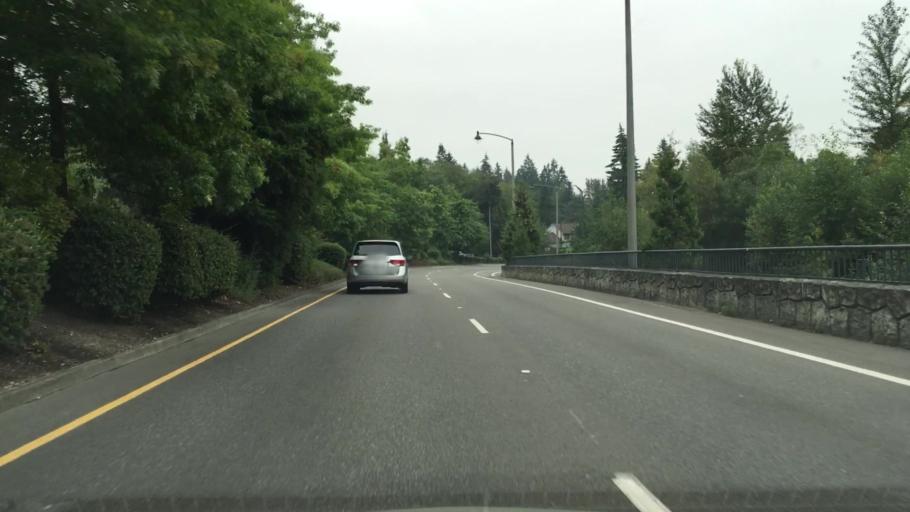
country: US
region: Washington
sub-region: King County
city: Newcastle
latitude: 47.5305
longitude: -122.1628
